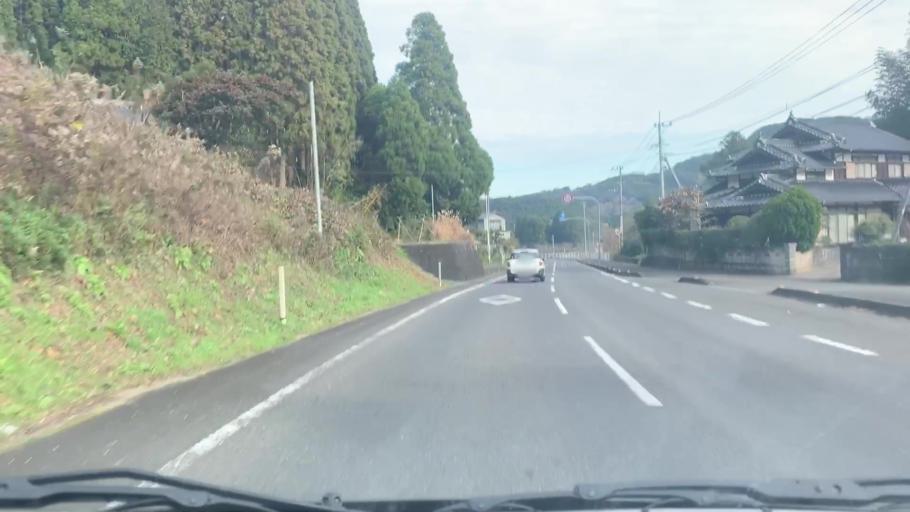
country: JP
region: Saga Prefecture
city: Imaricho-ko
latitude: 33.3209
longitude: 129.9691
